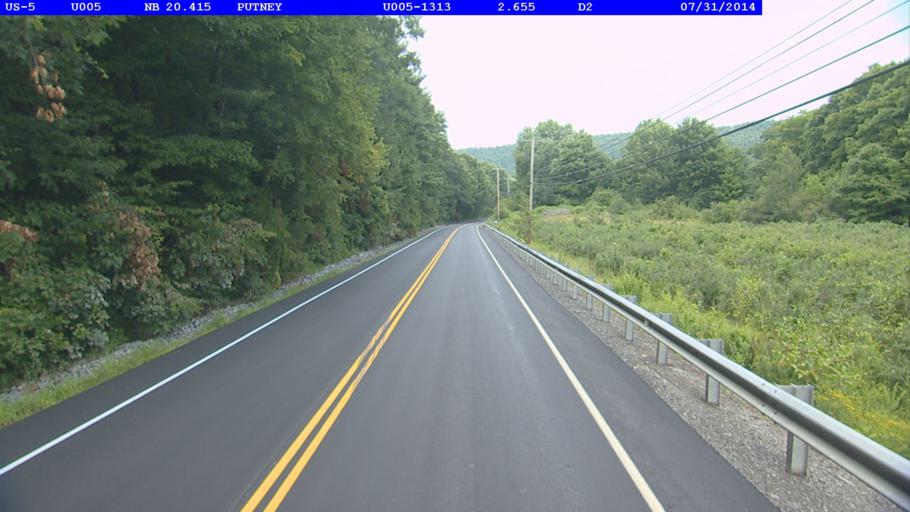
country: US
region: New Hampshire
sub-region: Cheshire County
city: Westmoreland
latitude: 42.9952
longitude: -72.4960
